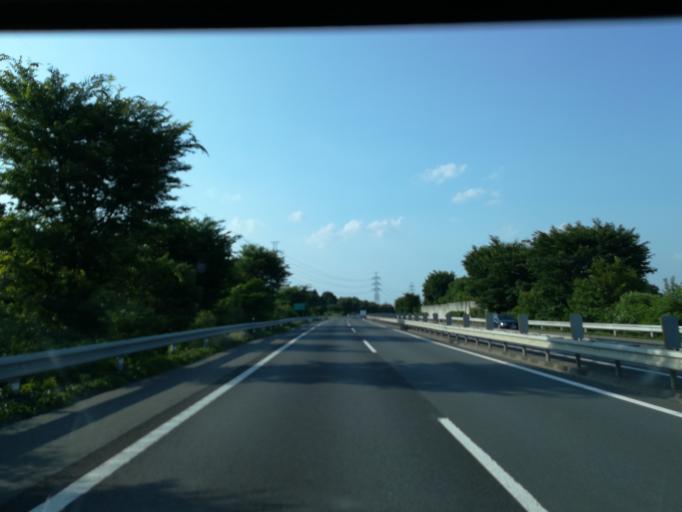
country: JP
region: Saitama
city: Sayama
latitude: 35.8903
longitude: 139.3877
